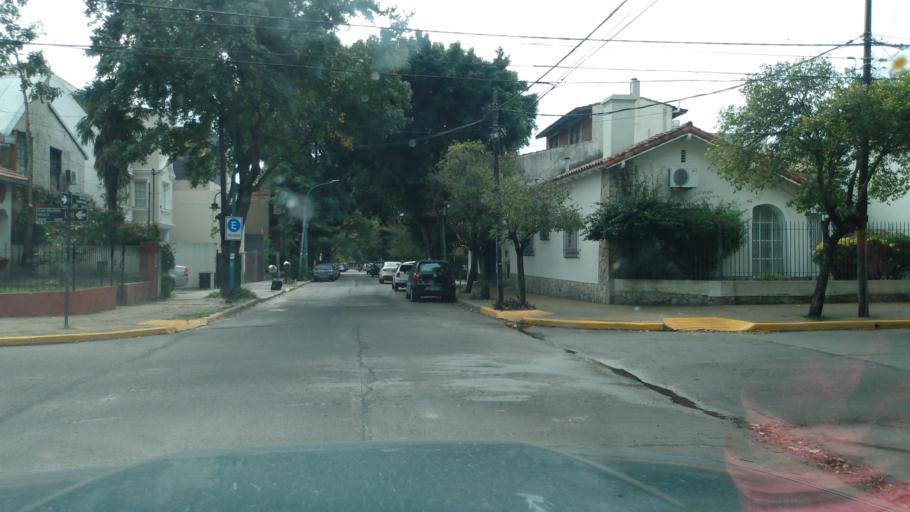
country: AR
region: Buenos Aires
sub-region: Partido de Vicente Lopez
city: Olivos
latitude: -34.5132
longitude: -58.4959
